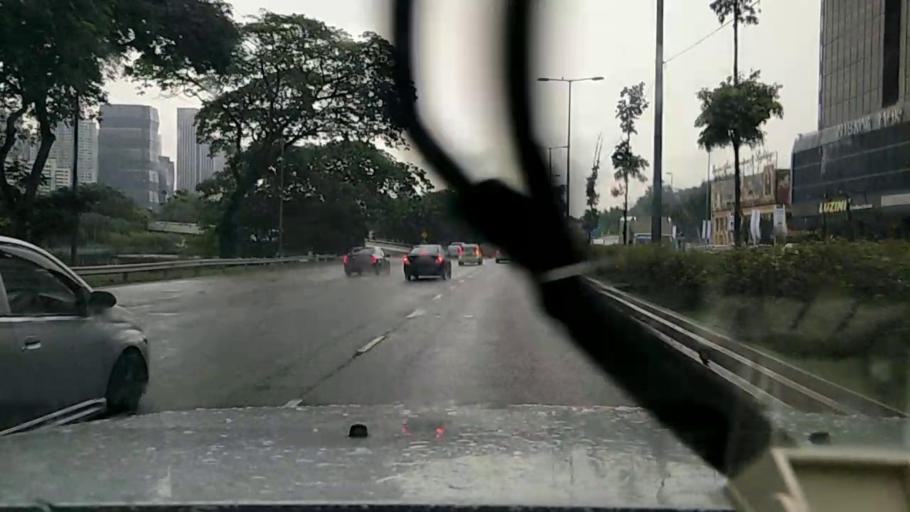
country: MY
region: Kuala Lumpur
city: Kuala Lumpur
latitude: 3.1225
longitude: 101.6807
